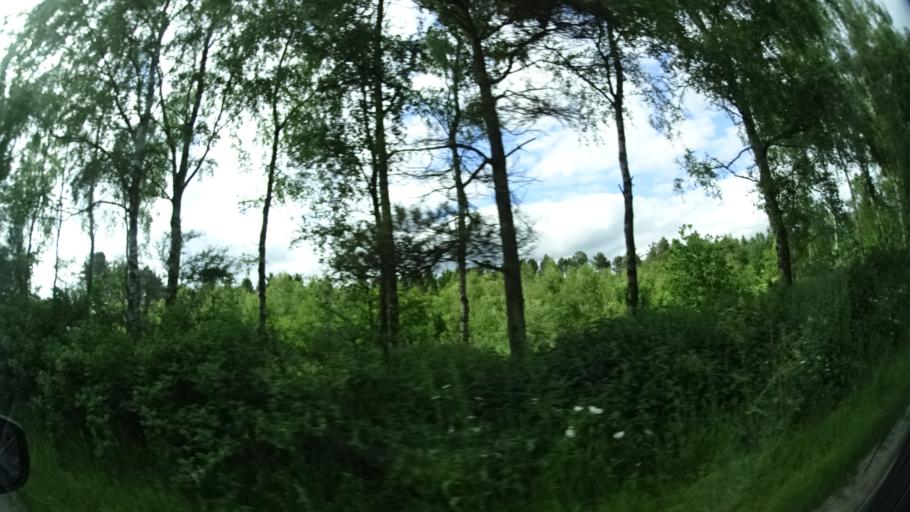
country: DK
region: Central Jutland
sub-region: Syddjurs Kommune
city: Ryomgard
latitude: 56.3520
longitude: 10.4770
